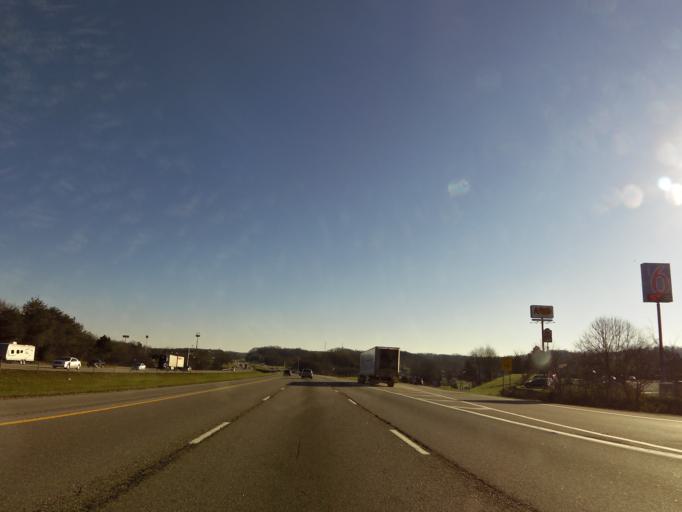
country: US
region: Tennessee
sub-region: Knox County
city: Mascot
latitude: 36.0027
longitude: -83.7800
